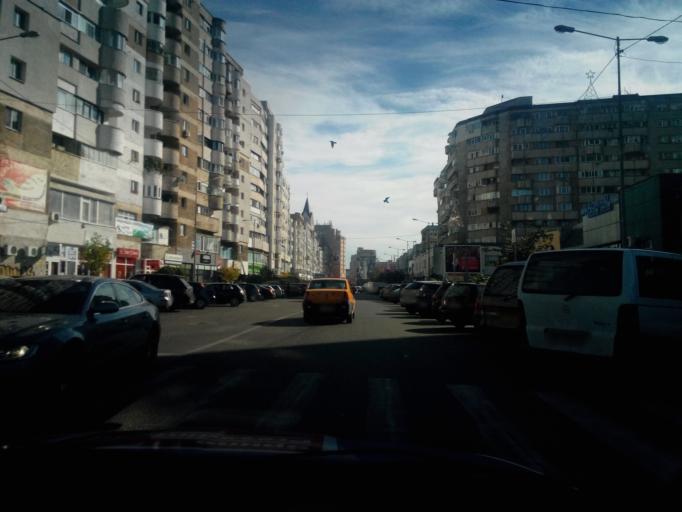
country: RO
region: Bacau
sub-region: Municipiul Bacau
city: Bacau
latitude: 46.5688
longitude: 26.9121
